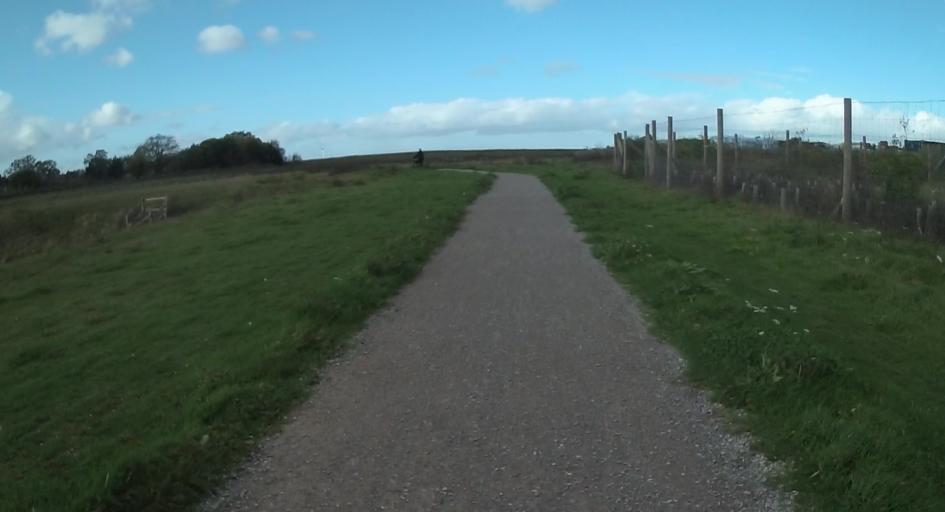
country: GB
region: England
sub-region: Wokingham
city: Shinfield
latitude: 51.4006
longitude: -0.9558
